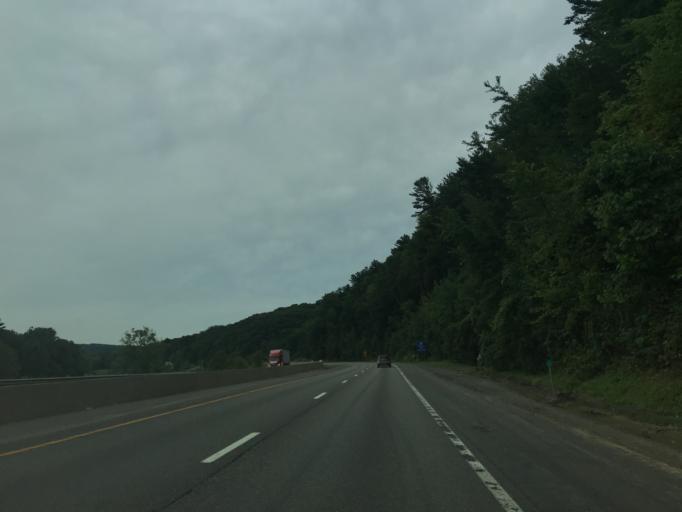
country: US
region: New York
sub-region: Broome County
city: Chenango Bridge
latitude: 42.1604
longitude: -75.8543
